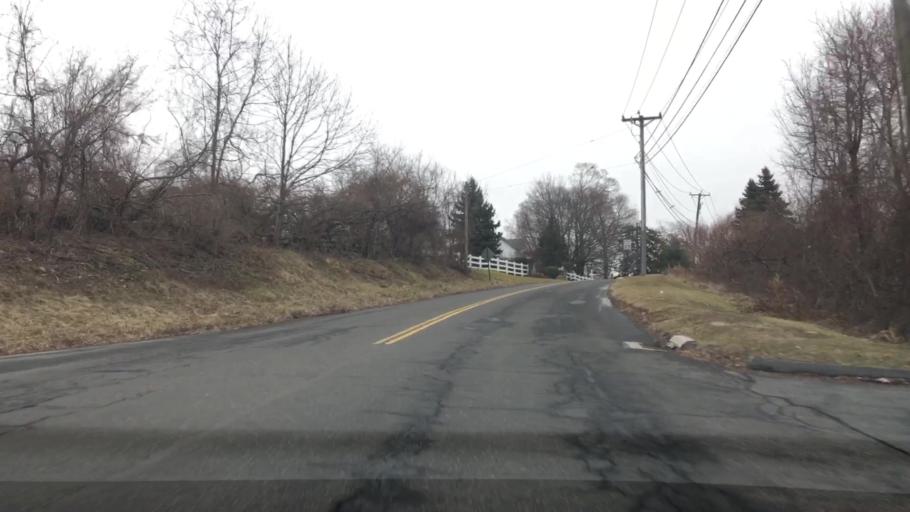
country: US
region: Connecticut
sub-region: Fairfield County
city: Bethel
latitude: 41.4399
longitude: -73.3871
